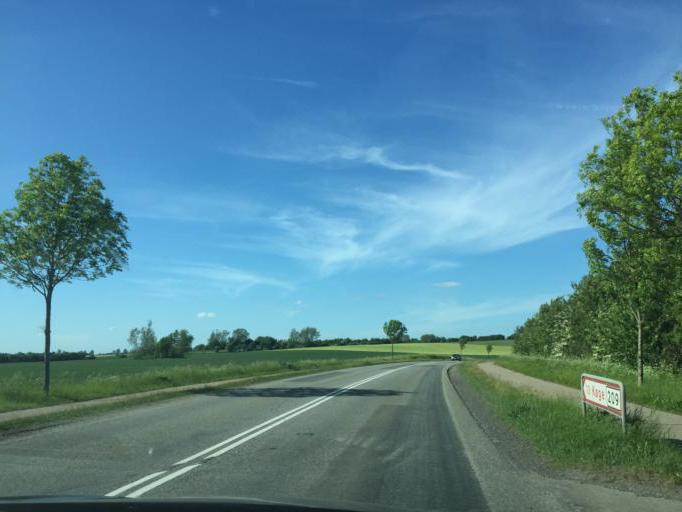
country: DK
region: Zealand
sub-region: Stevns Kommune
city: Harlev
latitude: 55.3586
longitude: 12.2489
